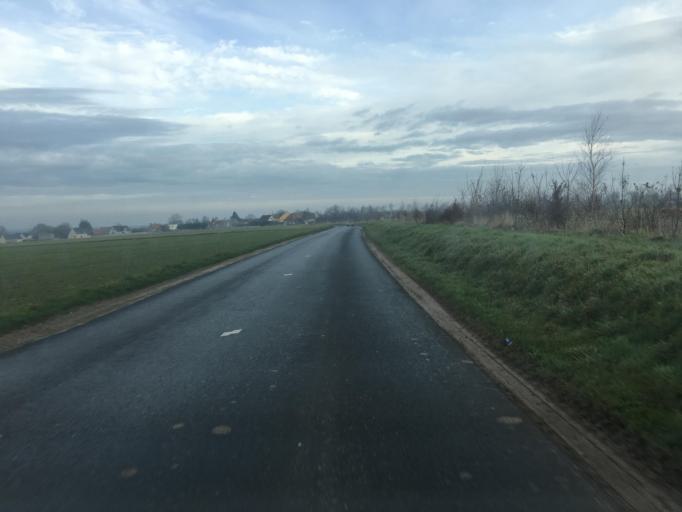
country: FR
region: Lower Normandy
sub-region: Departement du Calvados
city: Creully
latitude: 49.2439
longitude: -0.5697
